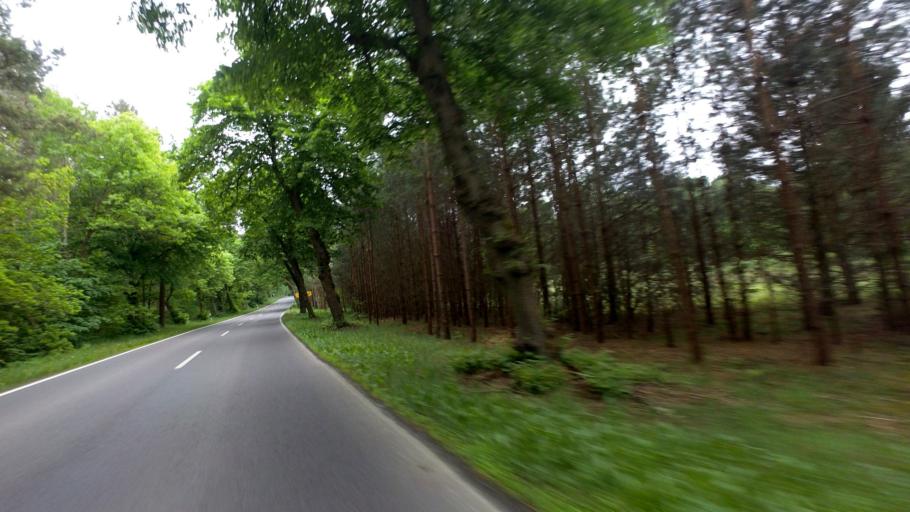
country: DE
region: Brandenburg
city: Templin
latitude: 53.0882
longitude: 13.5071
